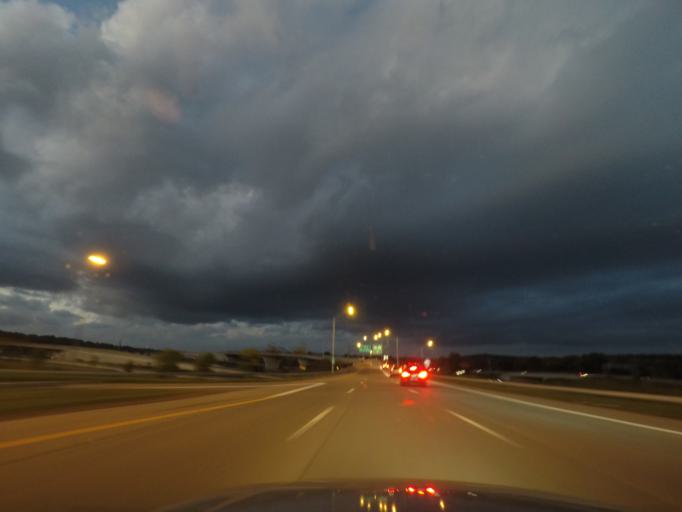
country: US
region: New York
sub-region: Orange County
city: Gardnertown
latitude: 41.5123
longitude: -74.0695
